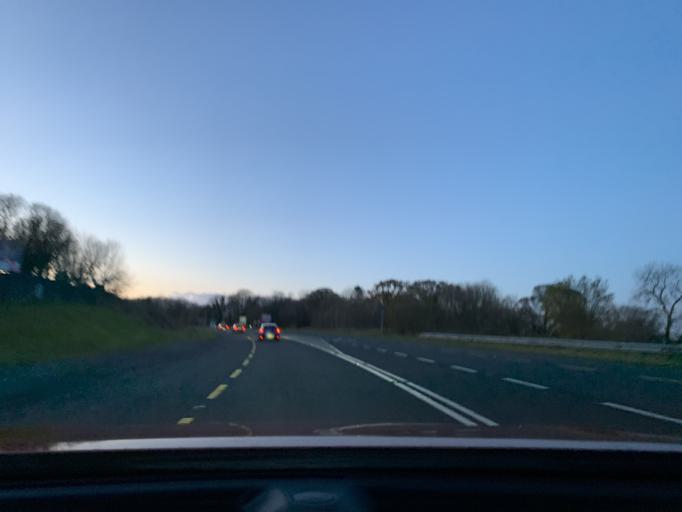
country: IE
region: Connaught
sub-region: Roscommon
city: Boyle
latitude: 53.9697
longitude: -8.2028
